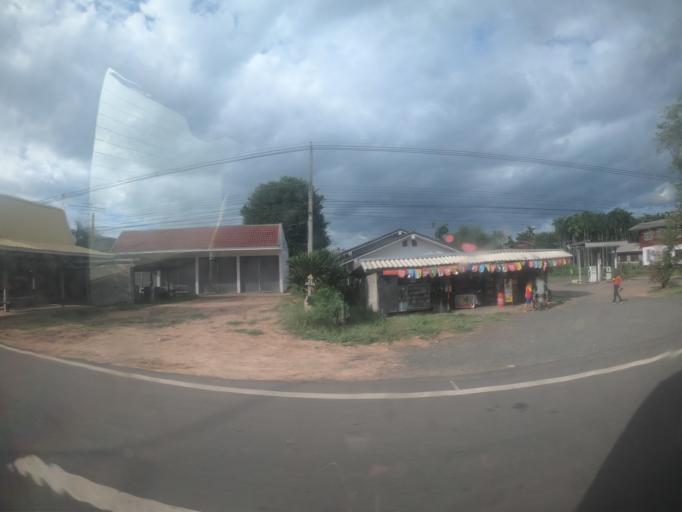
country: TH
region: Surin
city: Kap Choeng
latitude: 14.5269
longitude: 103.5351
